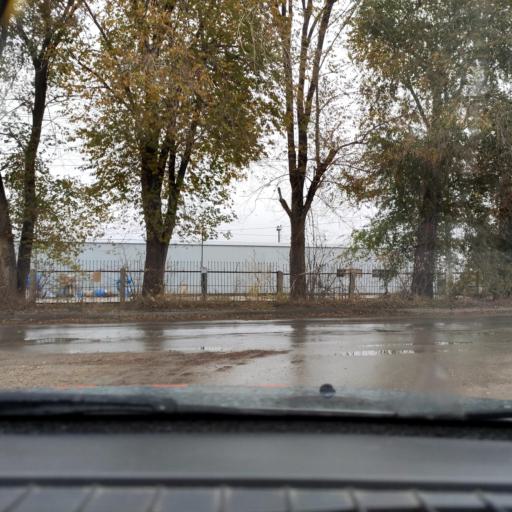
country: RU
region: Samara
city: Tol'yatti
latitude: 53.5705
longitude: 49.2833
